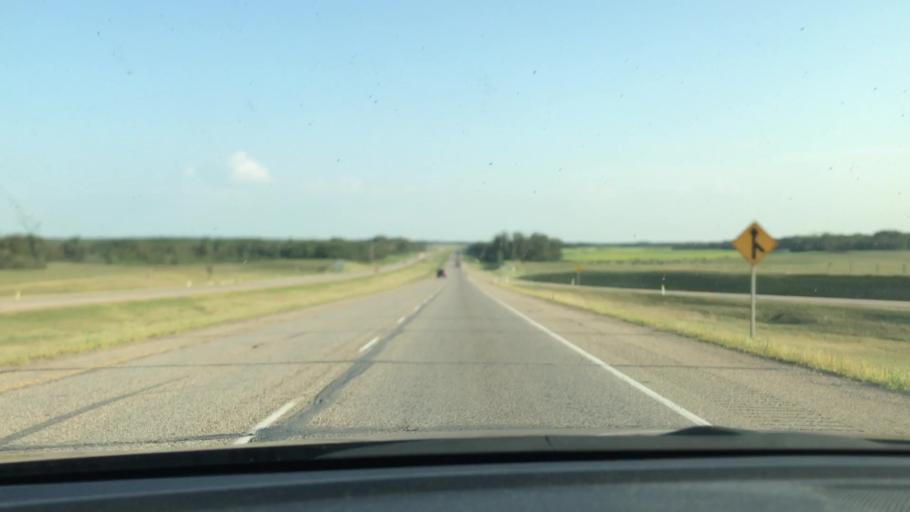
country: CA
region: Alberta
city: Ponoka
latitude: 52.5785
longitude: -113.6632
